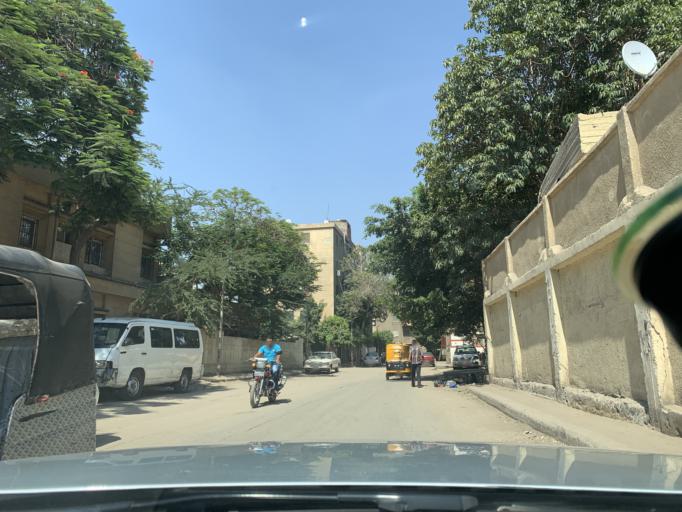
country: EG
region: Muhafazat al Qahirah
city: Cairo
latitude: 30.0777
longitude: 31.2588
